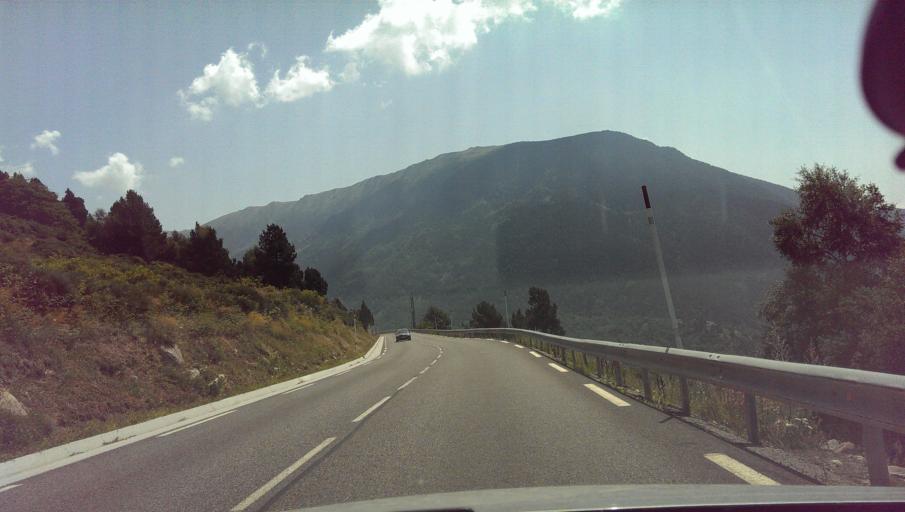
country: AD
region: Encamp
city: Pas de la Casa
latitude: 42.5527
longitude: 1.8215
